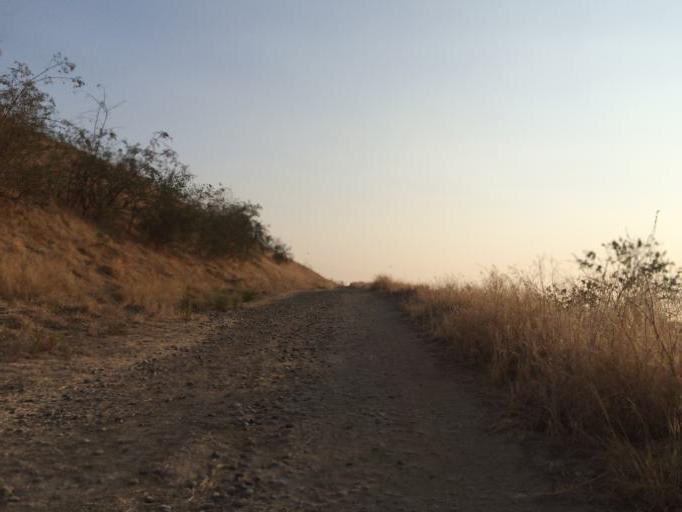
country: US
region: California
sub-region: Fresno County
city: Clovis
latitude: 36.8532
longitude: -119.8085
